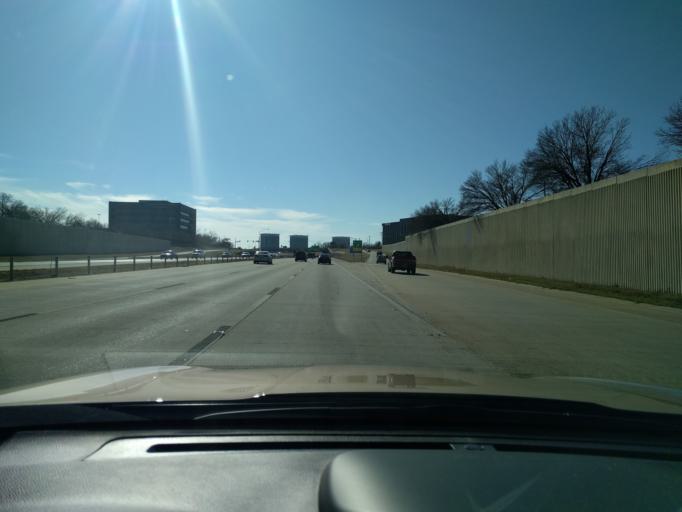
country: US
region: Oklahoma
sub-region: Oklahoma County
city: Nichols Hills
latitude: 35.5402
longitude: -97.5769
